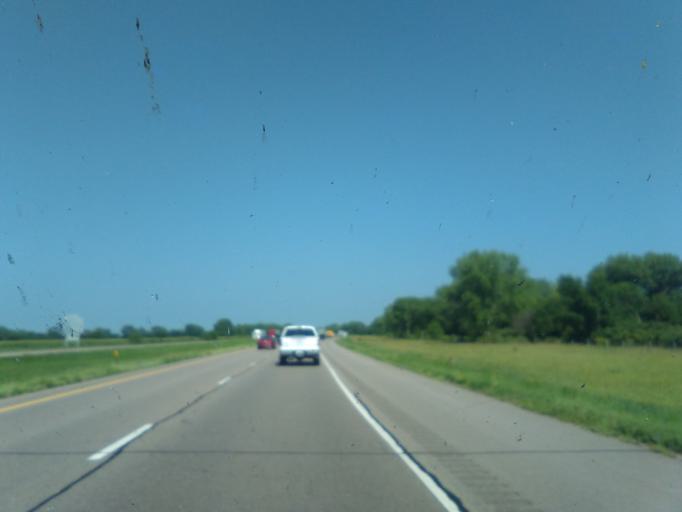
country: US
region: Nebraska
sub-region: Buffalo County
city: Gibbon
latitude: 40.6907
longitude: -98.9308
